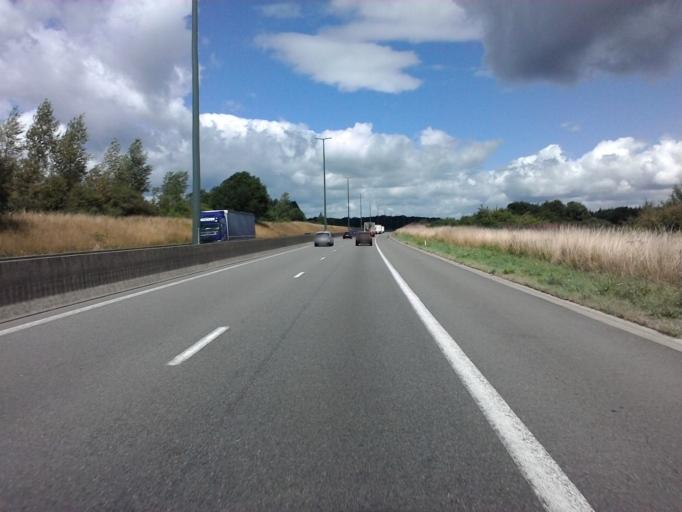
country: BE
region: Wallonia
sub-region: Province du Luxembourg
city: Habay-la-Vieille
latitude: 49.7246
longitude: 5.5860
